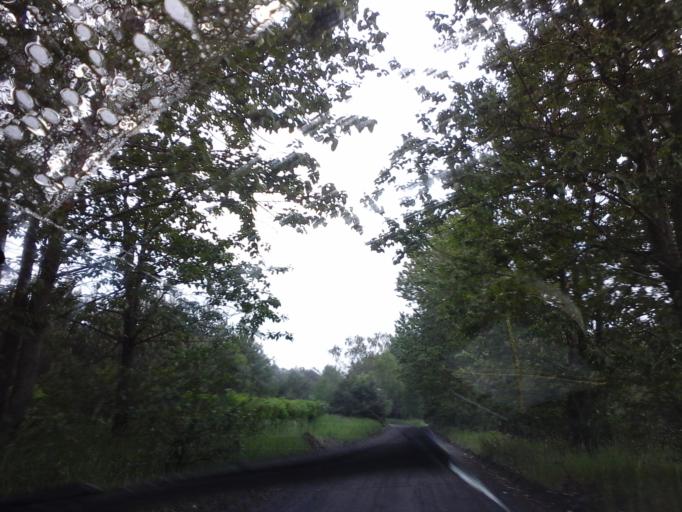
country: PL
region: West Pomeranian Voivodeship
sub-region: Powiat walecki
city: Miroslawiec
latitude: 53.2472
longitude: 16.0252
